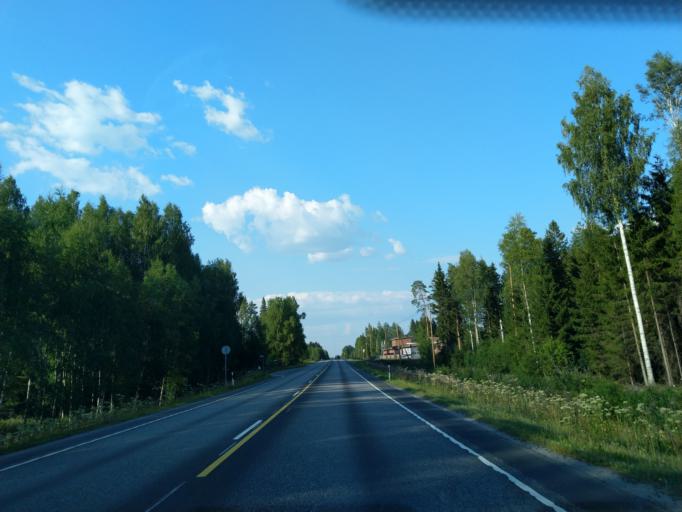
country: FI
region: Satakunta
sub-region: Pori
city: Pomarkku
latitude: 61.7268
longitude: 22.0648
